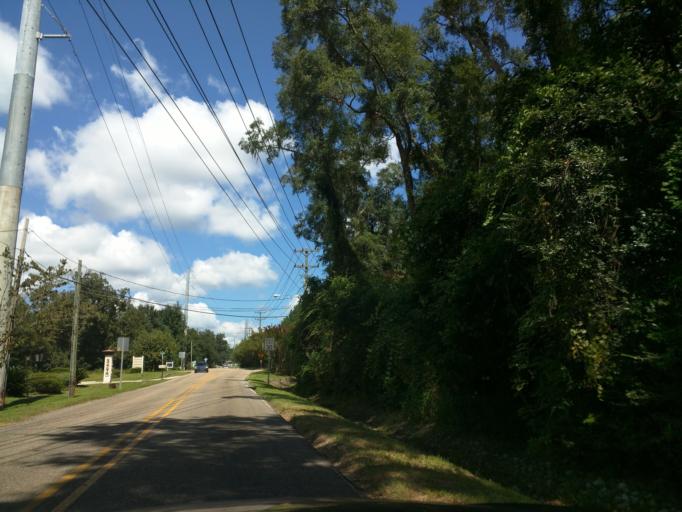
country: US
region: Florida
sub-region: Leon County
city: Tallahassee
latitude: 30.4568
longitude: -84.2224
